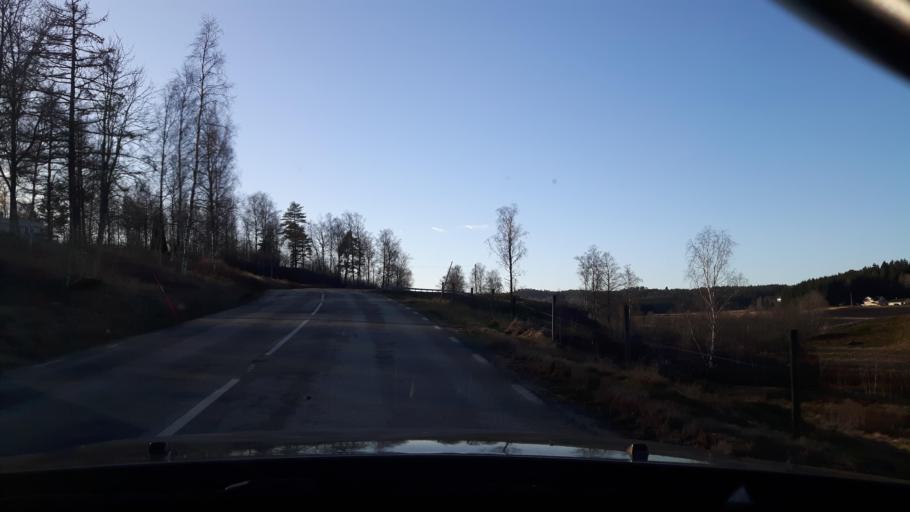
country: SE
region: Vaestra Goetaland
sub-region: Munkedals Kommun
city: Munkedal
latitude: 58.6201
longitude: 11.7669
